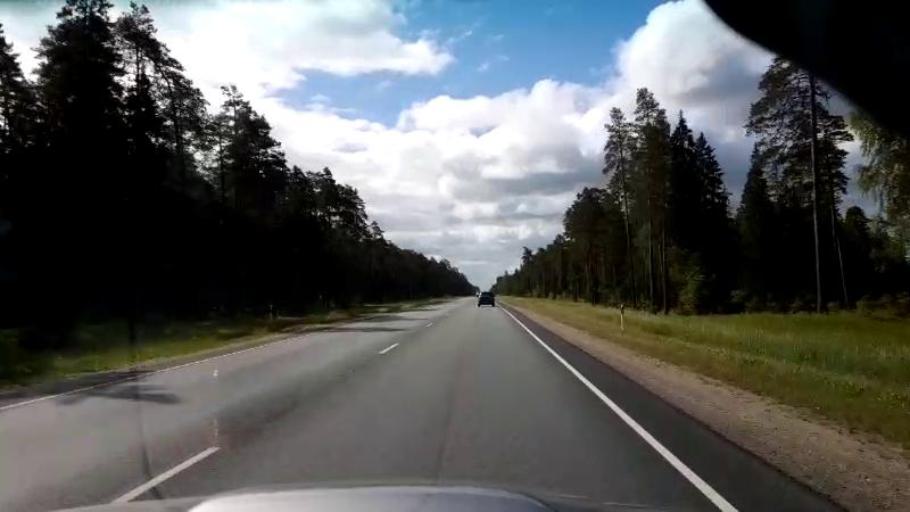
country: EE
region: Raplamaa
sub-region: Maerjamaa vald
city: Marjamaa
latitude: 59.0129
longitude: 24.4549
